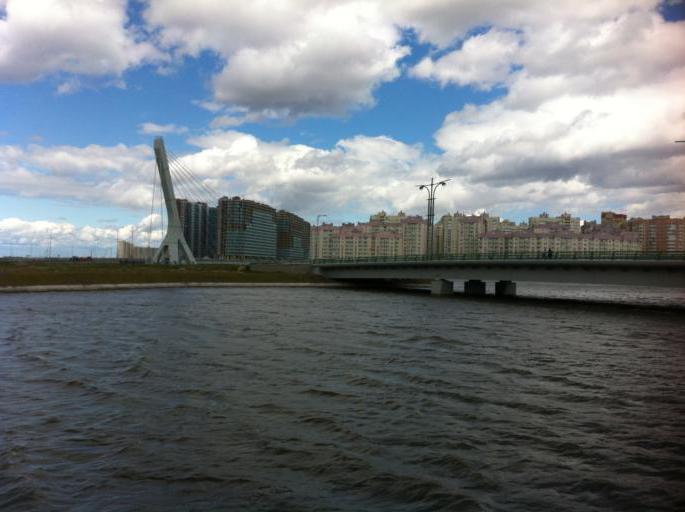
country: RU
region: St.-Petersburg
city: Sosnovaya Polyana
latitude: 59.8557
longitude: 30.1546
